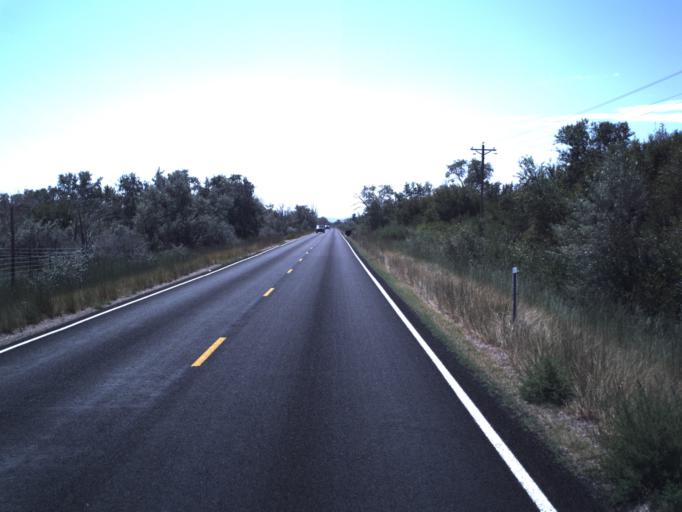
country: US
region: Utah
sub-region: Duchesne County
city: Roosevelt
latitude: 40.4283
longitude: -109.9264
